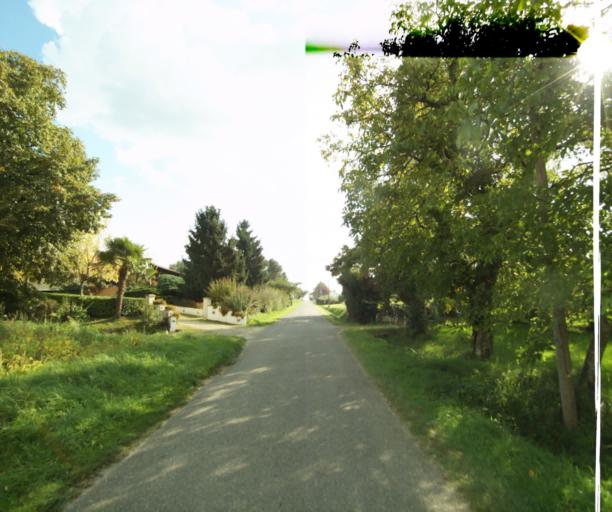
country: FR
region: Midi-Pyrenees
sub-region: Departement du Gers
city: Cazaubon
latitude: 43.8874
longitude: -0.0402
